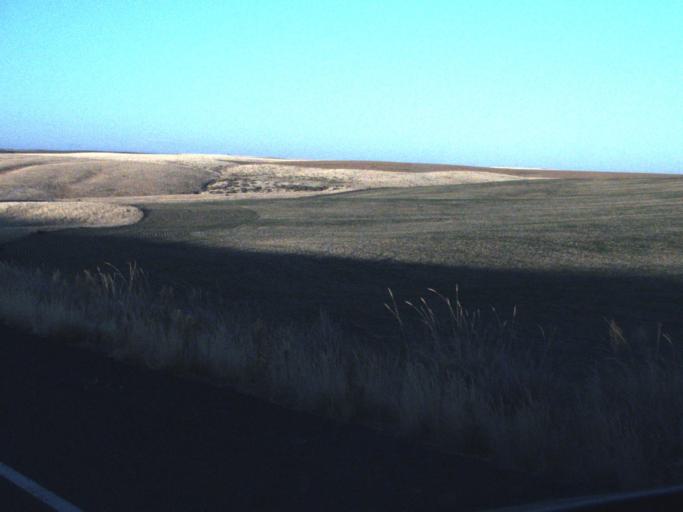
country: US
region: Washington
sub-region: Adams County
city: Ritzville
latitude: 46.9522
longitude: -118.5641
